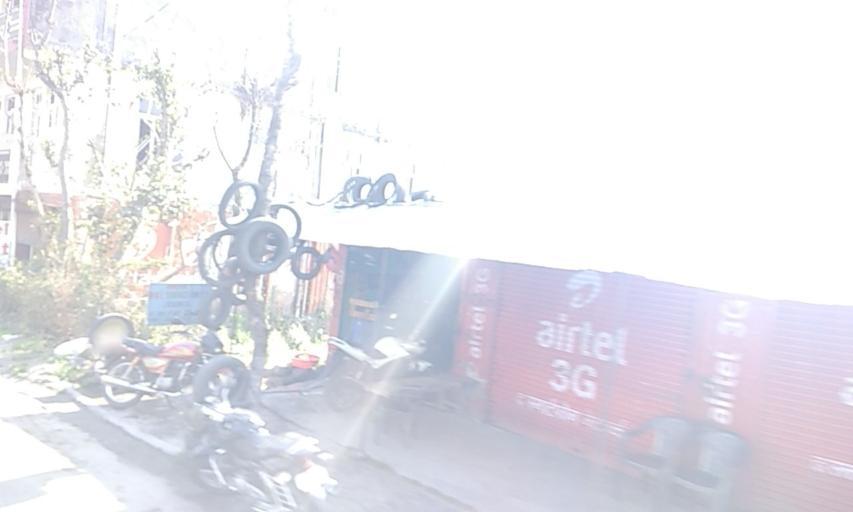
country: IN
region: Himachal Pradesh
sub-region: Kangra
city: Dharmsala
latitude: 32.1557
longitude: 76.4151
